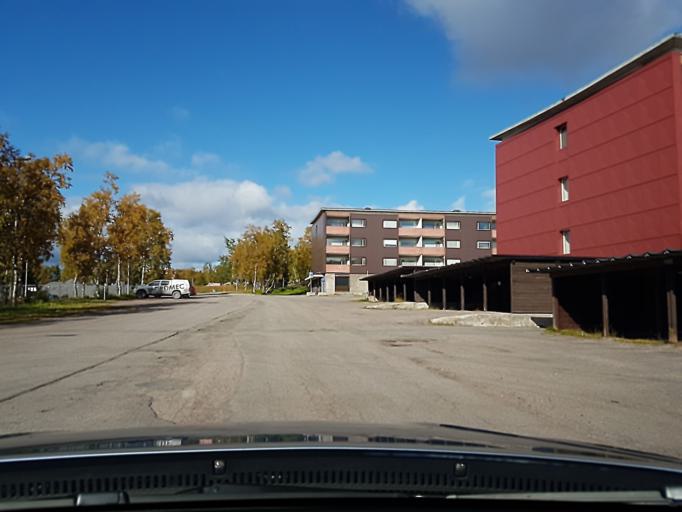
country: SE
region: Norrbotten
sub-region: Kiruna Kommun
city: Kiruna
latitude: 67.8479
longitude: 20.2254
